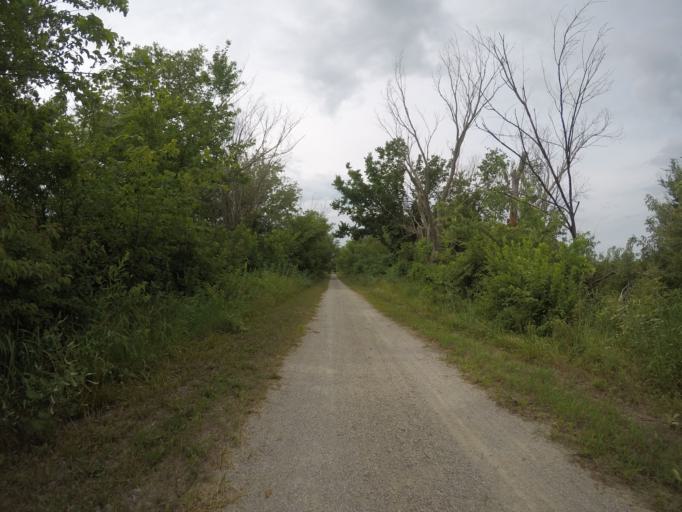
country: US
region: Kansas
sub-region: Franklin County
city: Ottawa
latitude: 38.5046
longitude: -95.2730
